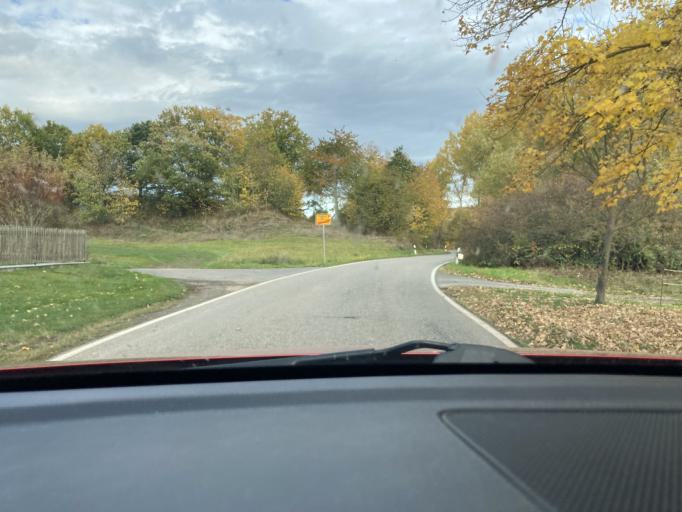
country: DE
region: Thuringia
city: Kleinbodungen
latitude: 51.4764
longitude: 10.5480
